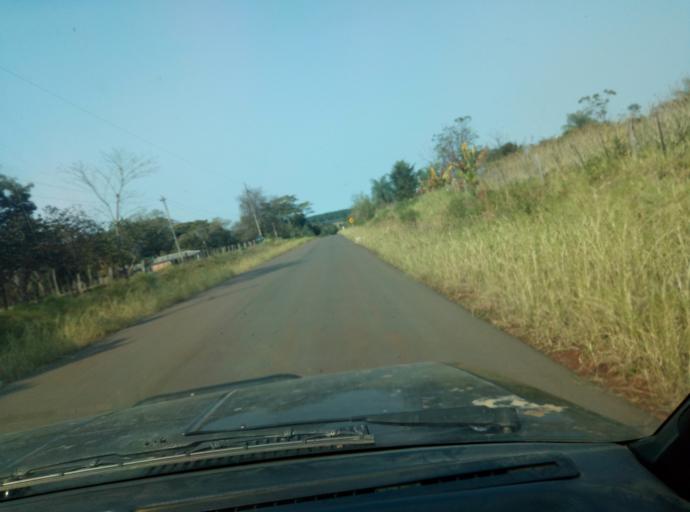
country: PY
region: Caaguazu
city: Carayao
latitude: -25.2358
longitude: -56.2869
